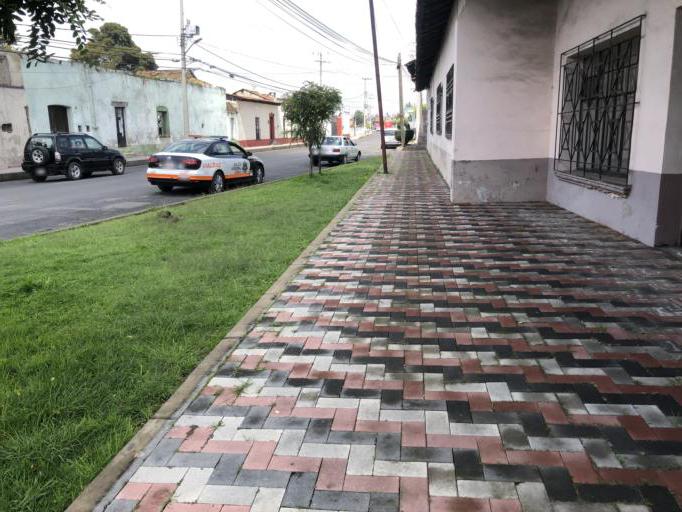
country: MX
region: Mexico
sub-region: Lerma
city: Nueva Ameyalco
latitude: 19.2851
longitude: -99.5024
